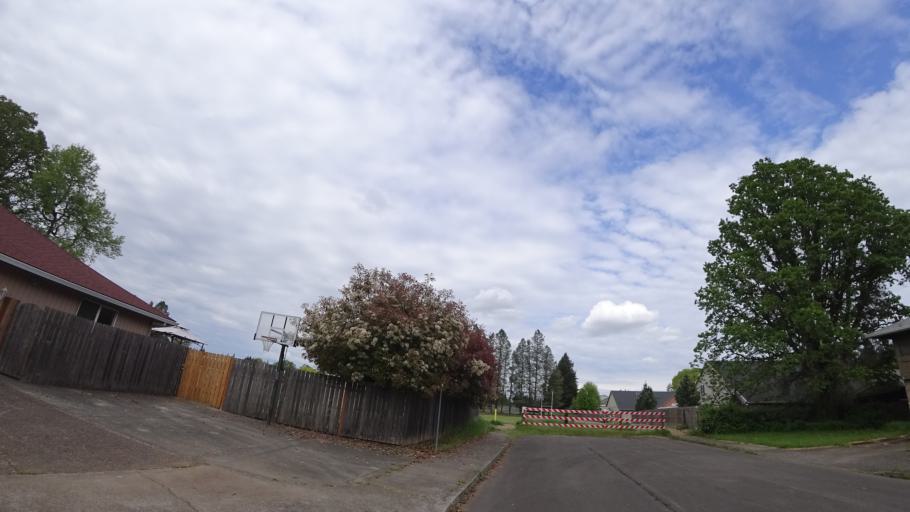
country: US
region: Oregon
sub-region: Washington County
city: Hillsboro
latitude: 45.4926
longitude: -122.9589
